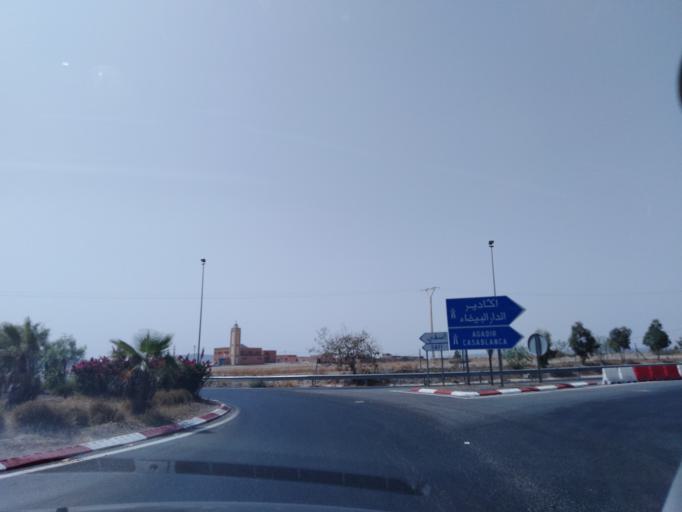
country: MA
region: Marrakech-Tensift-Al Haouz
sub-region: Marrakech
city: Marrakesh
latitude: 31.7733
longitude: -8.1306
